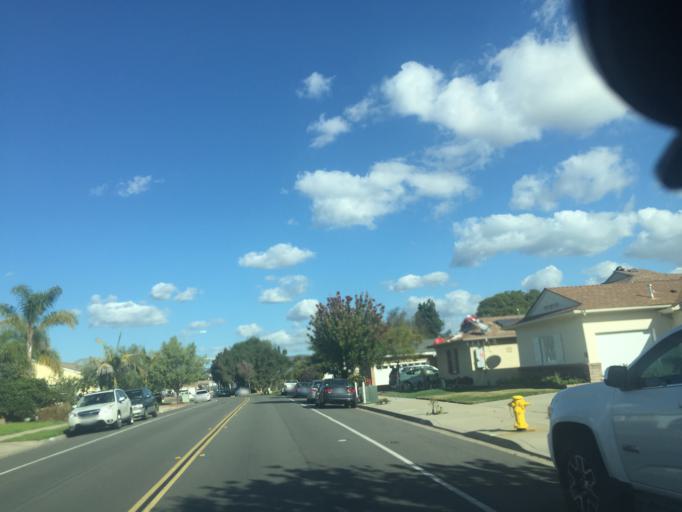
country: US
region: California
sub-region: San Diego County
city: La Mesa
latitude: 32.7895
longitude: -117.0861
